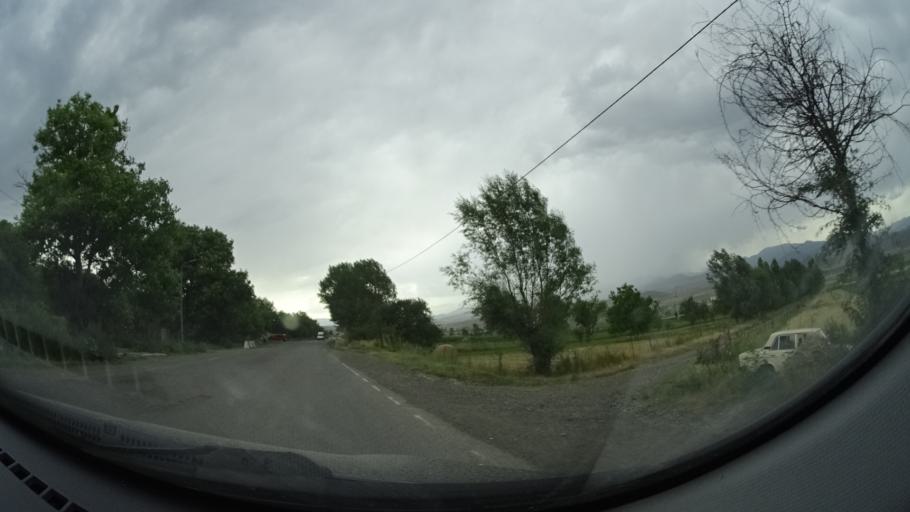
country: GE
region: Samtskhe-Javakheti
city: Akhaltsikhe
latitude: 41.6376
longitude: 43.0363
